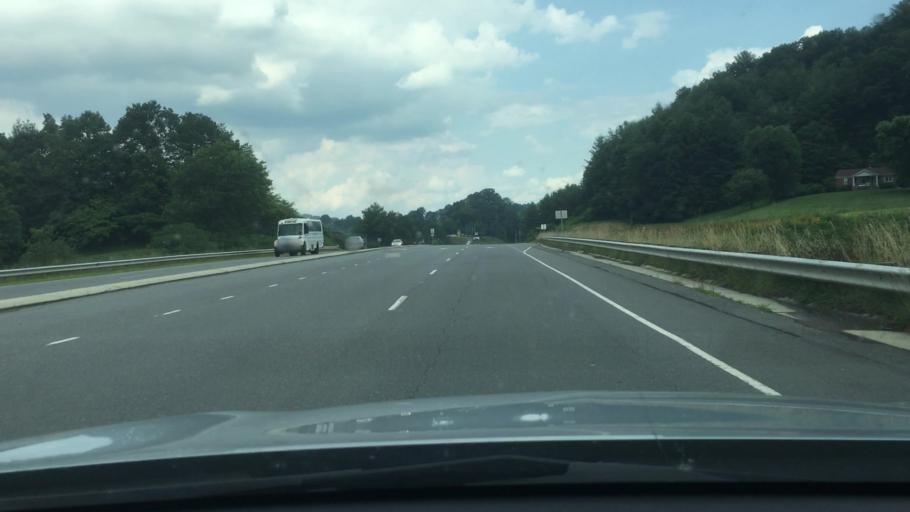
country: US
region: North Carolina
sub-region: Yancey County
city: Burnsville
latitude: 35.9108
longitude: -82.3741
